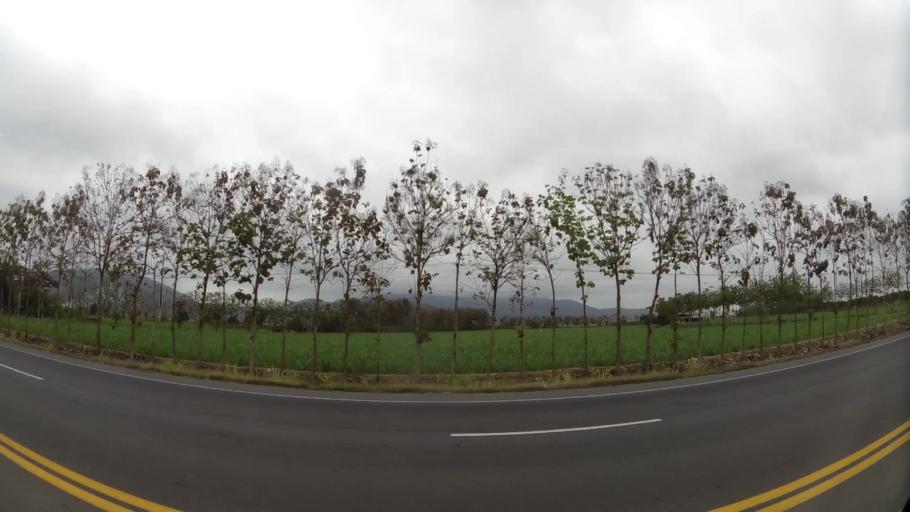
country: EC
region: Guayas
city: Naranjal
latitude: -2.4851
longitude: -79.6140
